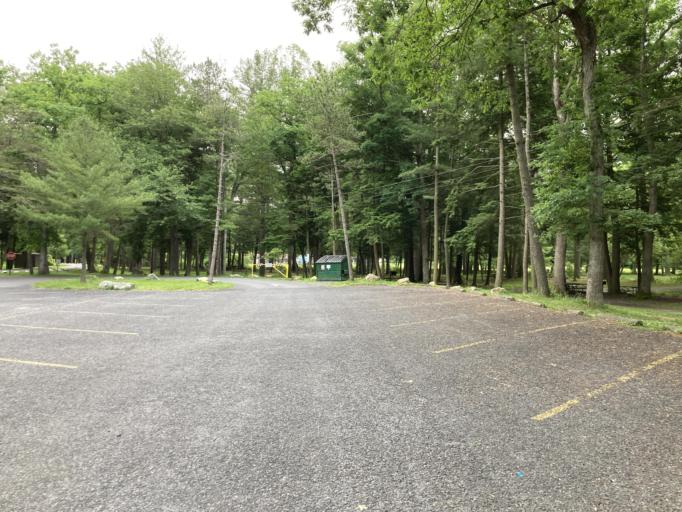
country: US
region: Pennsylvania
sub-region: Franklin County
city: Fayetteville
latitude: 39.9090
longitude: -77.4834
